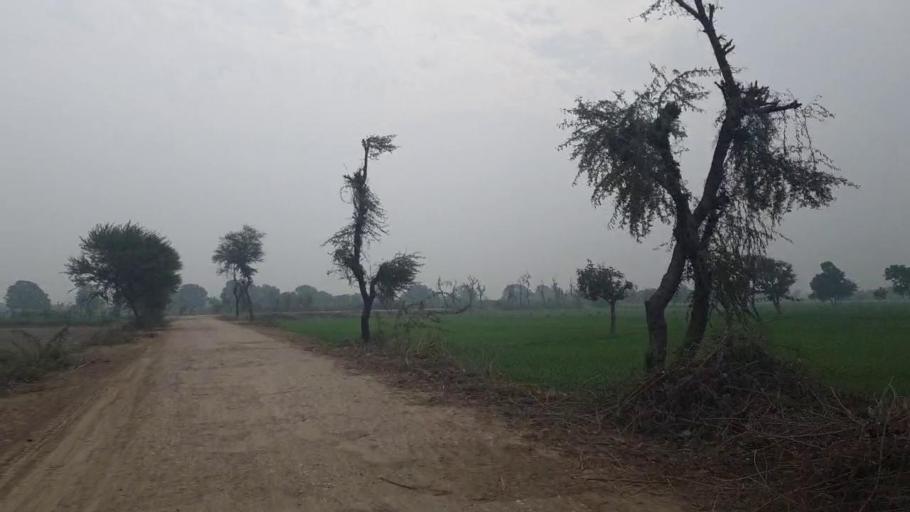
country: PK
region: Sindh
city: Tando Adam
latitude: 25.7081
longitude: 68.6170
